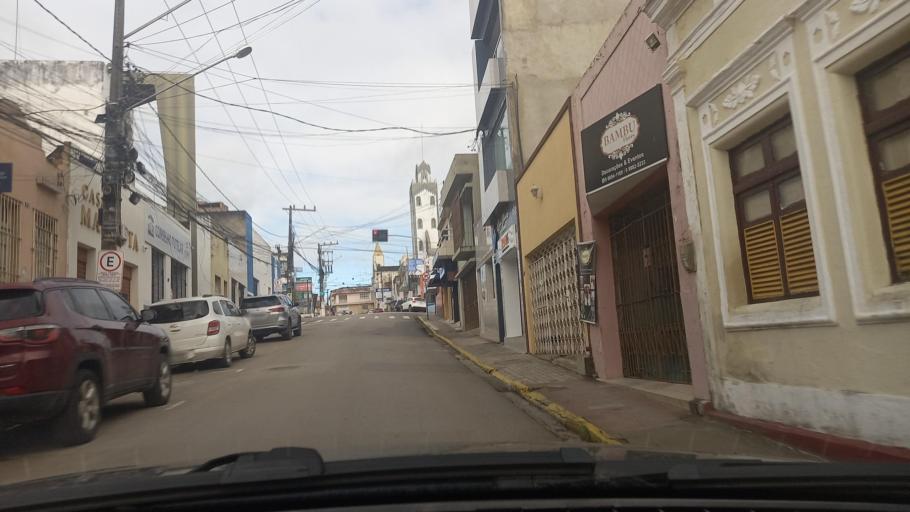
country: BR
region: Pernambuco
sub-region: Vitoria De Santo Antao
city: Vitoria de Santo Antao
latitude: -8.1190
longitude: -35.2974
